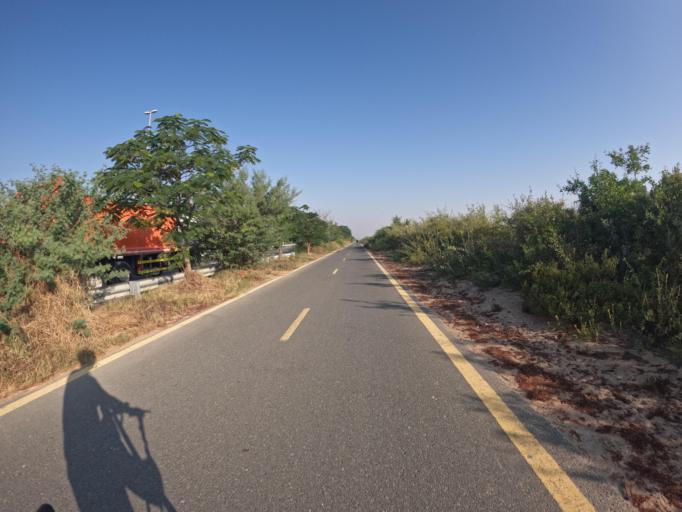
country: AE
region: Dubai
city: Dubai
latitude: 24.9103
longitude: 55.3420
